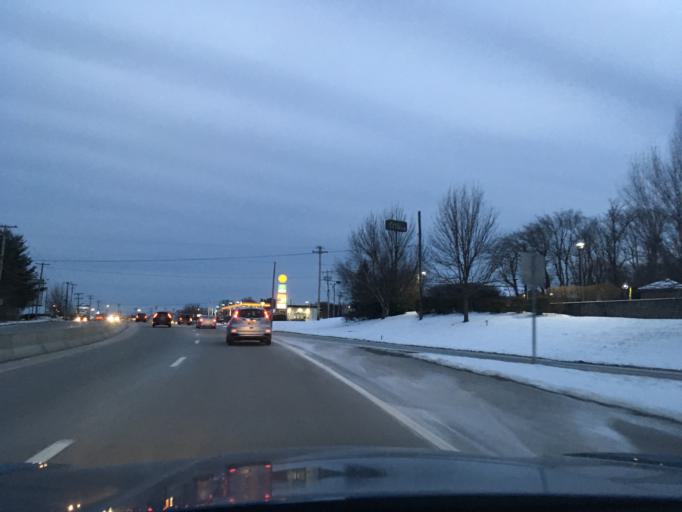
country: US
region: Rhode Island
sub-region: Kent County
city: West Warwick
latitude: 41.6656
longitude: -71.4994
